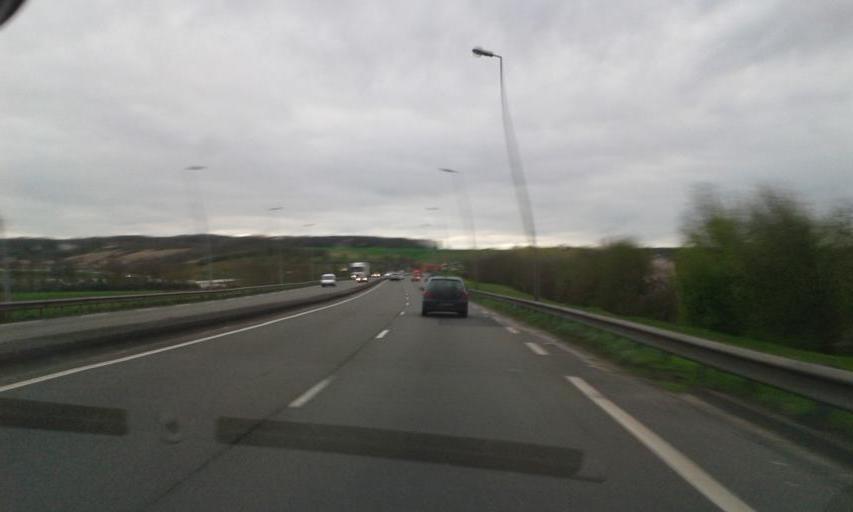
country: FR
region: Centre
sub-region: Departement d'Eure-et-Loir
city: Vernouillet
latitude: 48.7158
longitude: 1.3528
